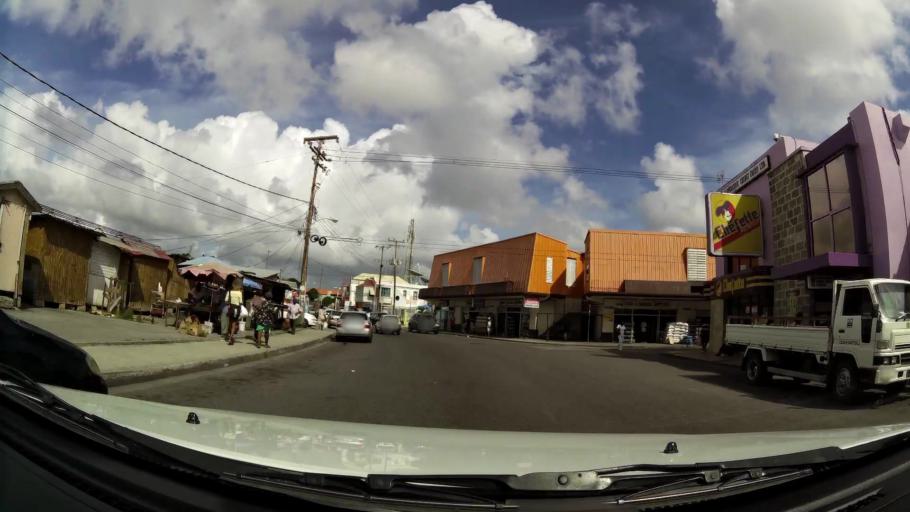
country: BB
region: Saint Michael
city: Bridgetown
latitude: 13.0959
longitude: -59.6116
